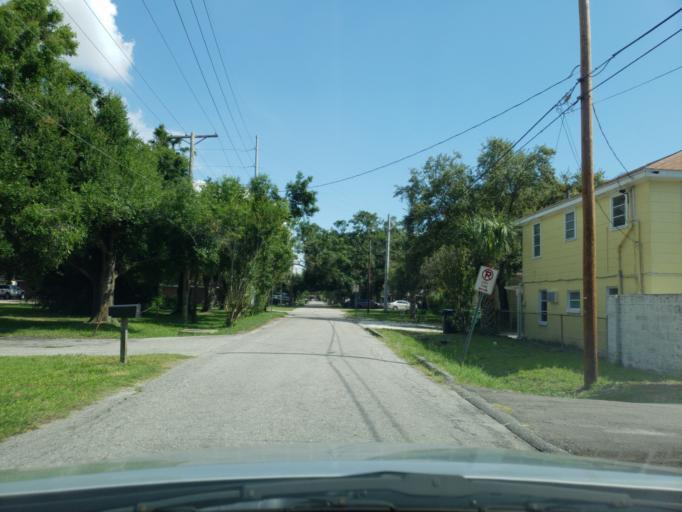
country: US
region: Florida
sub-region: Hillsborough County
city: Egypt Lake-Leto
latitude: 27.9768
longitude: -82.4959
